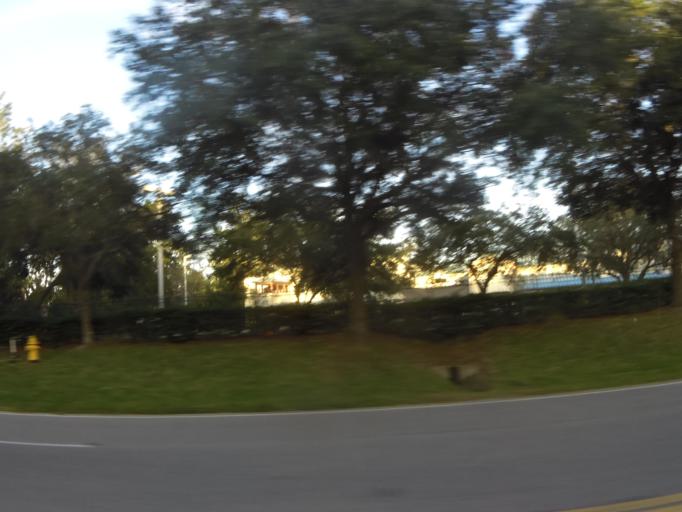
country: US
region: Florida
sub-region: Saint Johns County
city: Palm Valley
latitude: 30.1790
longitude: -81.3892
